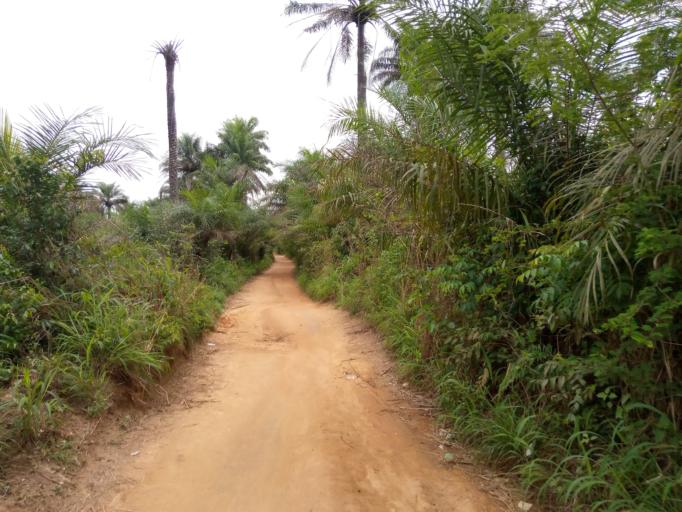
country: SL
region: Western Area
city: Waterloo
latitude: 8.3958
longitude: -12.9463
